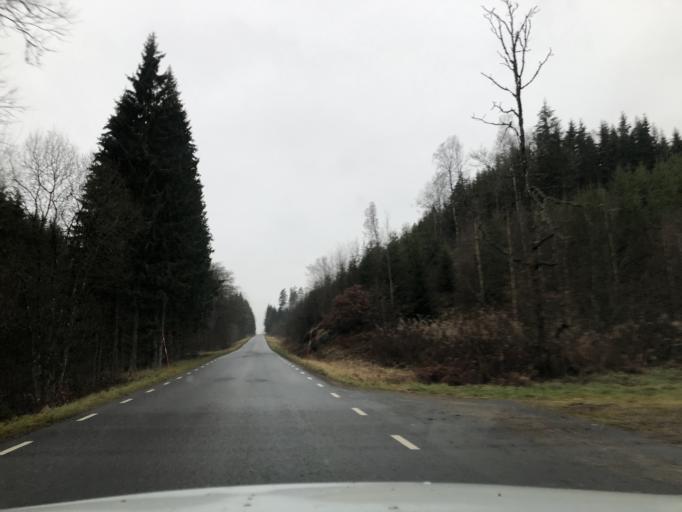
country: SE
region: Vaestra Goetaland
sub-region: Ulricehamns Kommun
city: Ulricehamn
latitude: 57.8320
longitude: 13.4034
